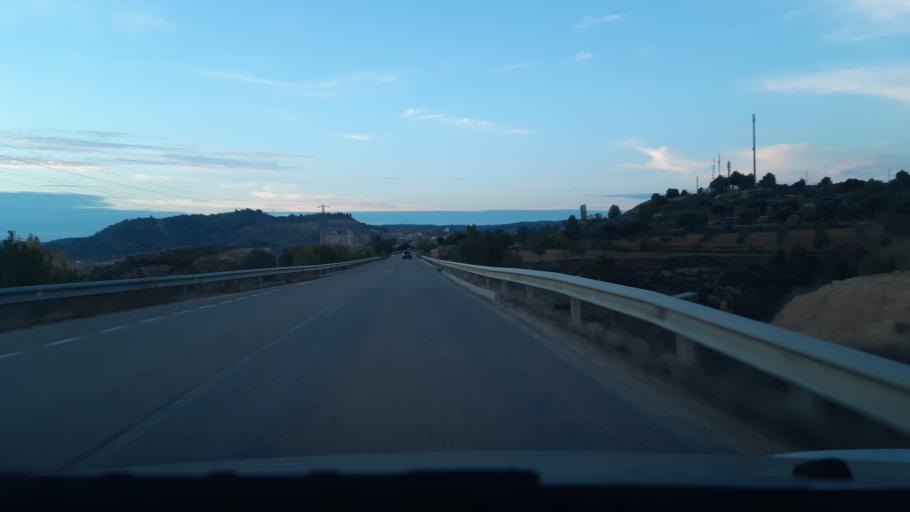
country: ES
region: Aragon
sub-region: Provincia de Teruel
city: Valderrobres
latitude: 40.8669
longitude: 0.1627
